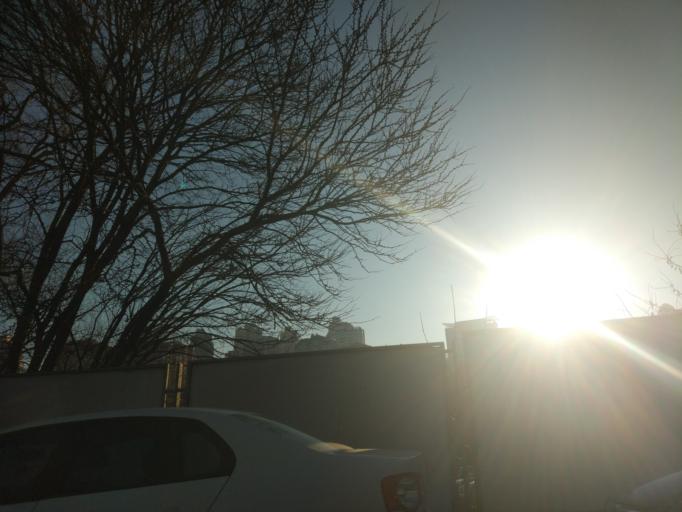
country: TR
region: Istanbul
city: Esenyurt
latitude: 41.0698
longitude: 28.6881
